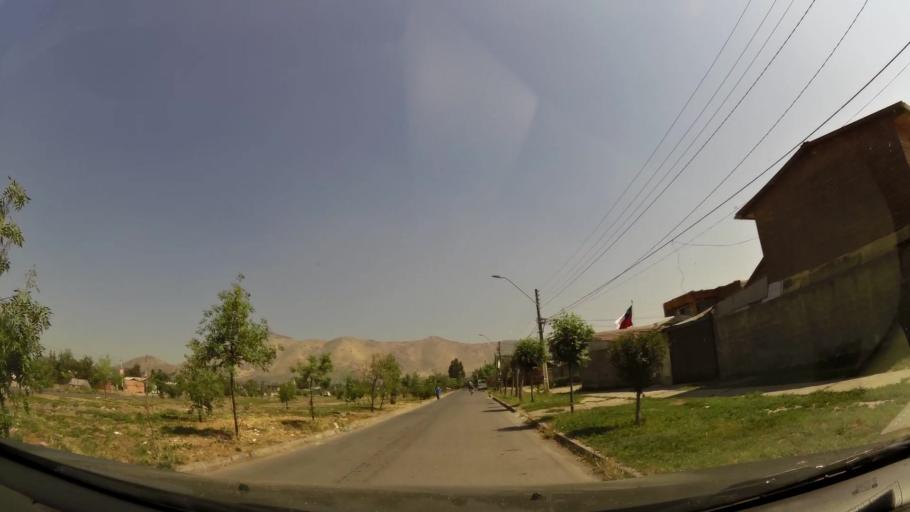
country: CL
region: Santiago Metropolitan
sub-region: Provincia de Maipo
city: San Bernardo
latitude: -33.5782
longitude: -70.7078
